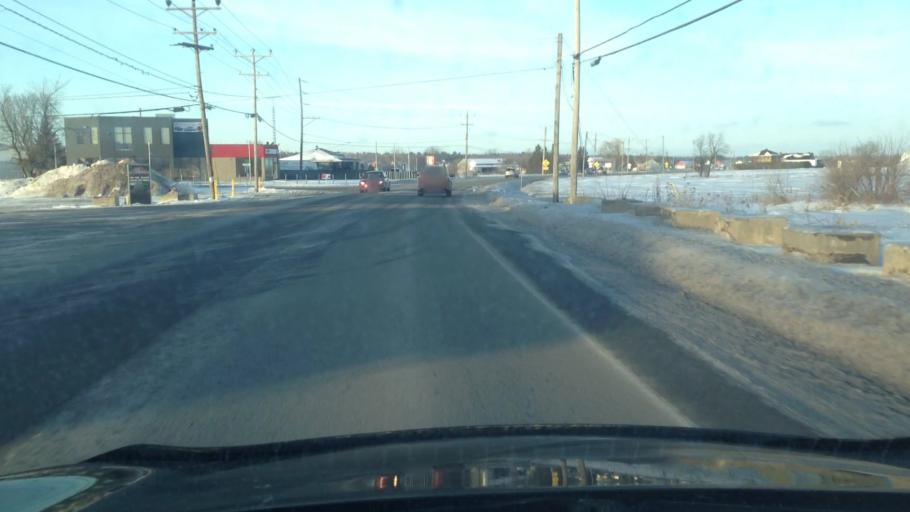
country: CA
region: Quebec
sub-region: Lanaudiere
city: Saint-Lin-Laurentides
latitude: 45.8882
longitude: -73.7579
